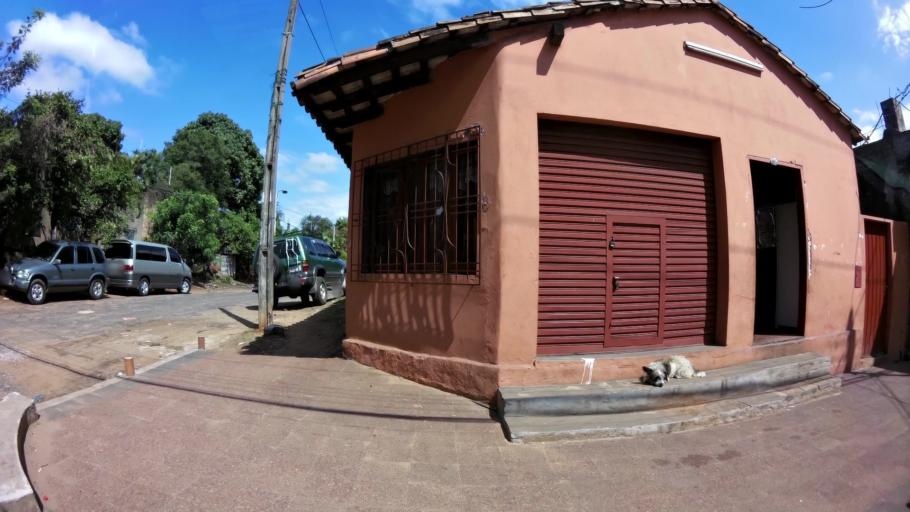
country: PY
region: Central
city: San Lorenzo
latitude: -25.2571
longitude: -57.4895
